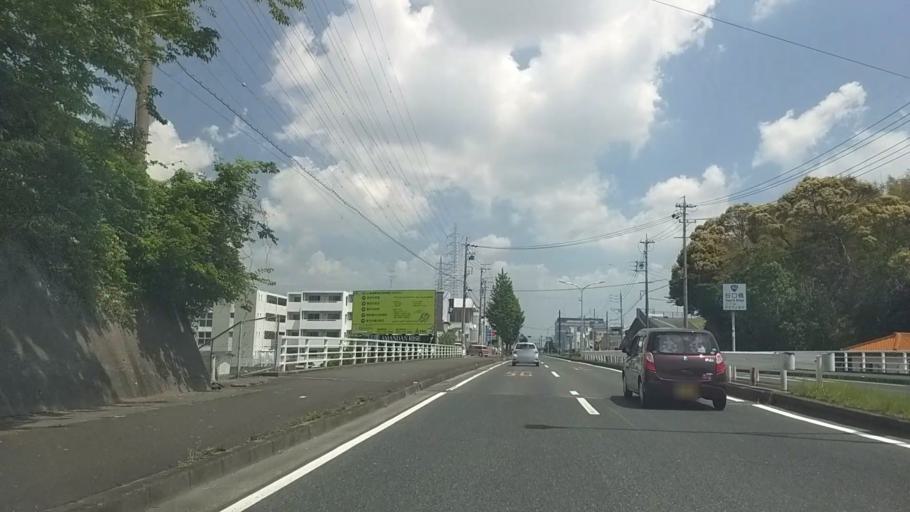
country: JP
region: Shizuoka
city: Hamamatsu
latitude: 34.7383
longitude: 137.7366
